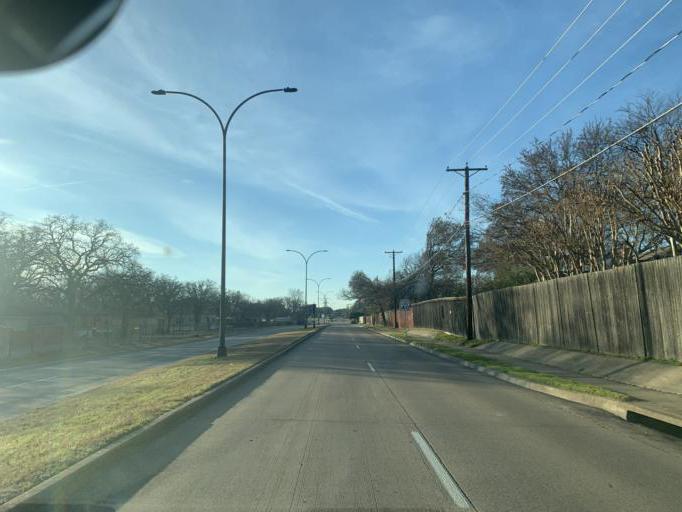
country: US
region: Texas
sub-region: Tarrant County
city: Arlington
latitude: 32.7700
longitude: -97.0737
